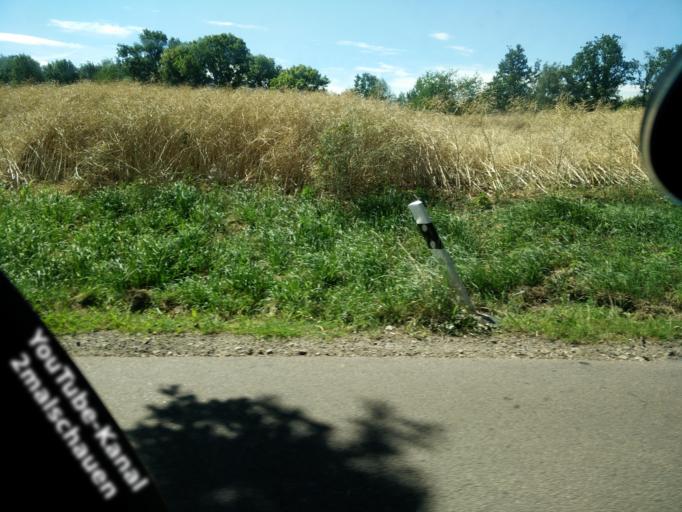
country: DE
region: Saxony
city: Dobeln
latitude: 51.1097
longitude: 13.0816
